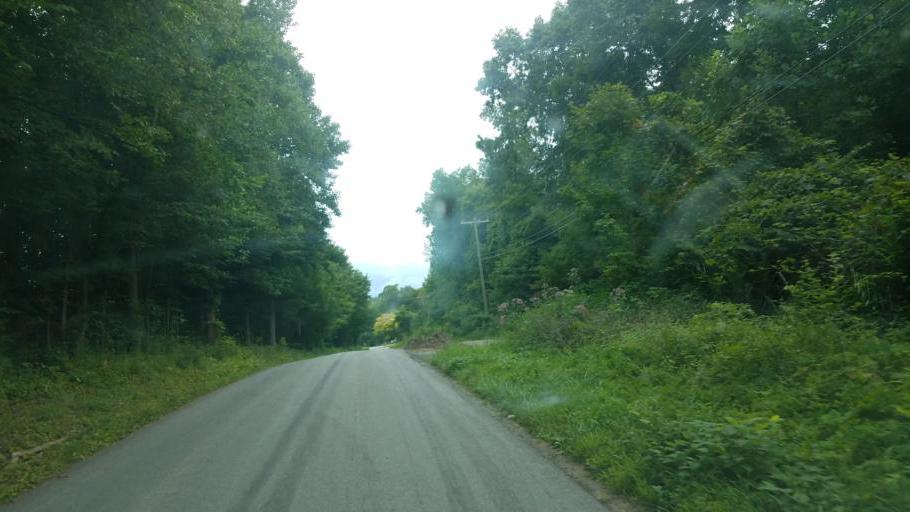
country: US
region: Pennsylvania
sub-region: Erie County
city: Lake City
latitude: 41.9988
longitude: -80.4307
